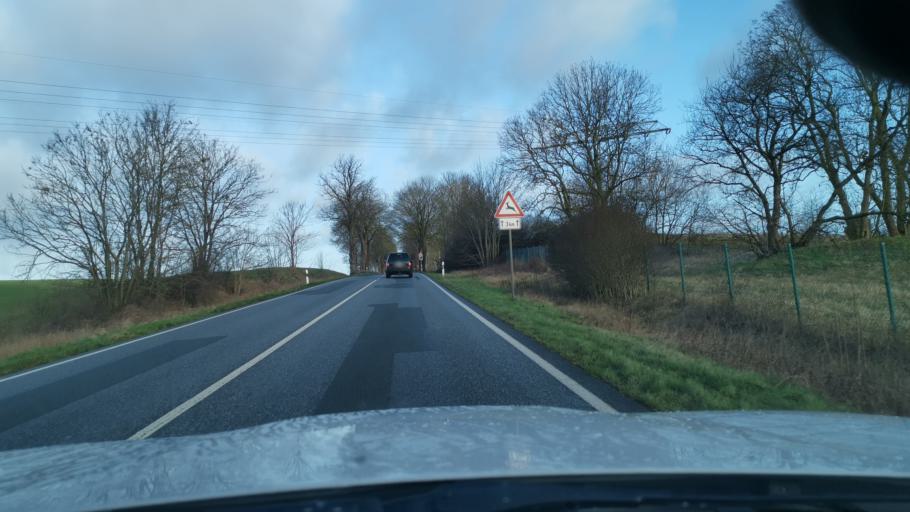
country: DE
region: Mecklenburg-Vorpommern
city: Laage
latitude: 53.9405
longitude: 12.3140
